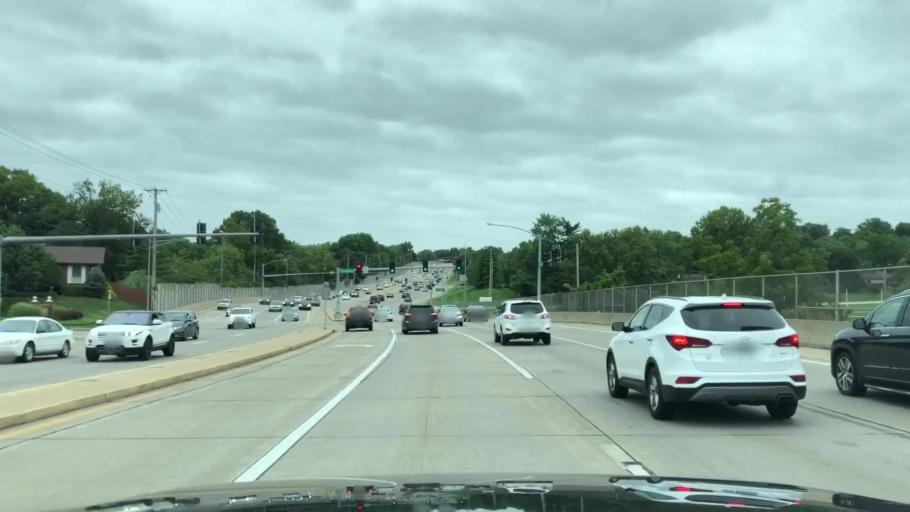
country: US
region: Missouri
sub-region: Saint Louis County
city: Manchester
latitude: 38.6081
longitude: -90.5107
